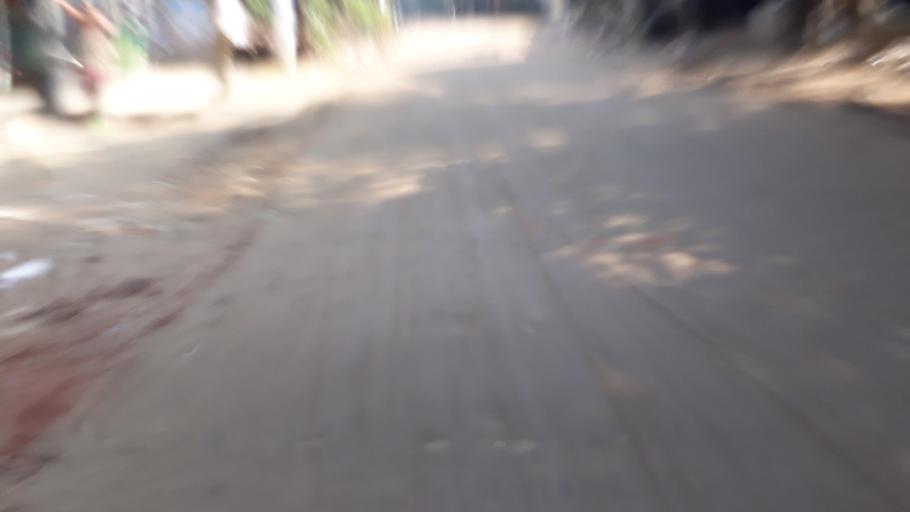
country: BD
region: Dhaka
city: Tungi
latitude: 23.8547
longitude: 90.3003
